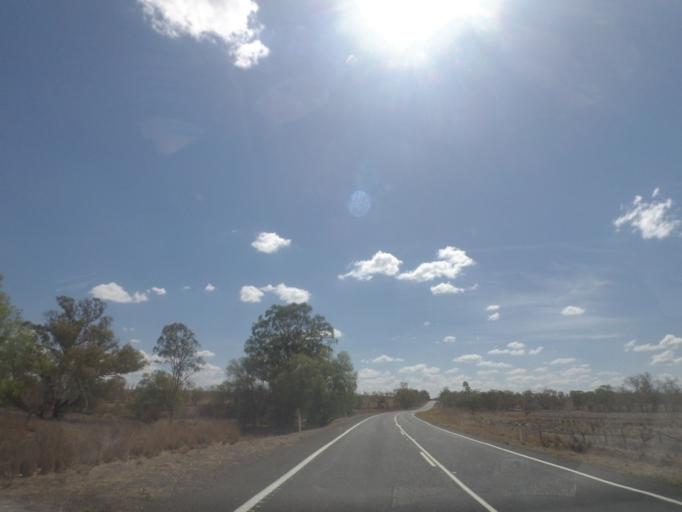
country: AU
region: Queensland
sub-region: Southern Downs
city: Warwick
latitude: -28.2058
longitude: 151.5821
